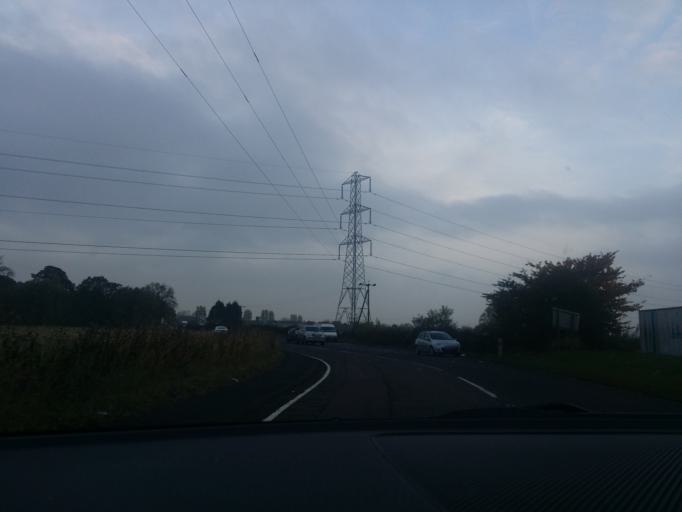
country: GB
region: Scotland
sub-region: Falkirk
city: Airth
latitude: 56.0589
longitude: -3.7613
